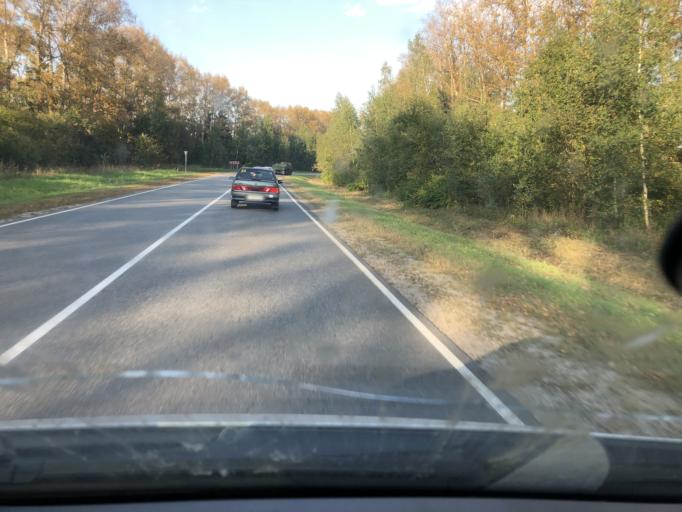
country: RU
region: Kaluga
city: Peremyshl'
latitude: 54.2417
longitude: 36.0760
